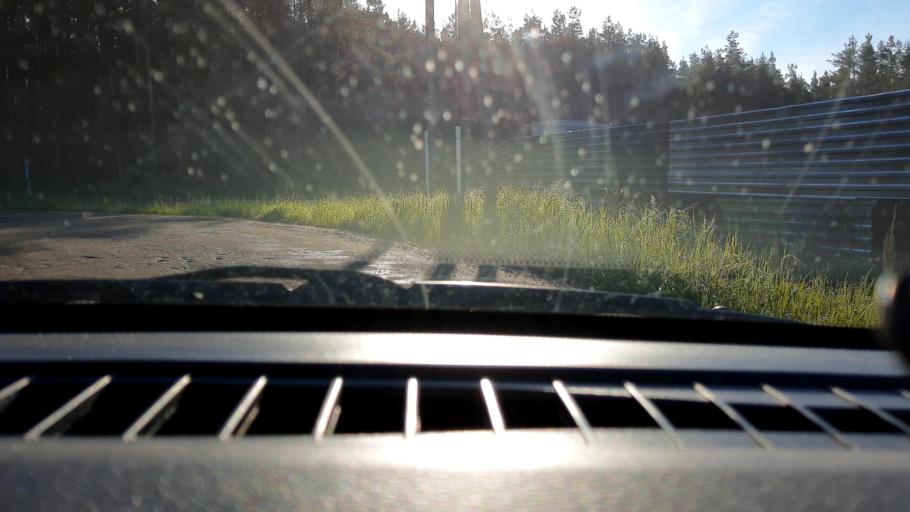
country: RU
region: Nizjnij Novgorod
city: Gorbatovka
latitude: 56.3050
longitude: 43.7404
